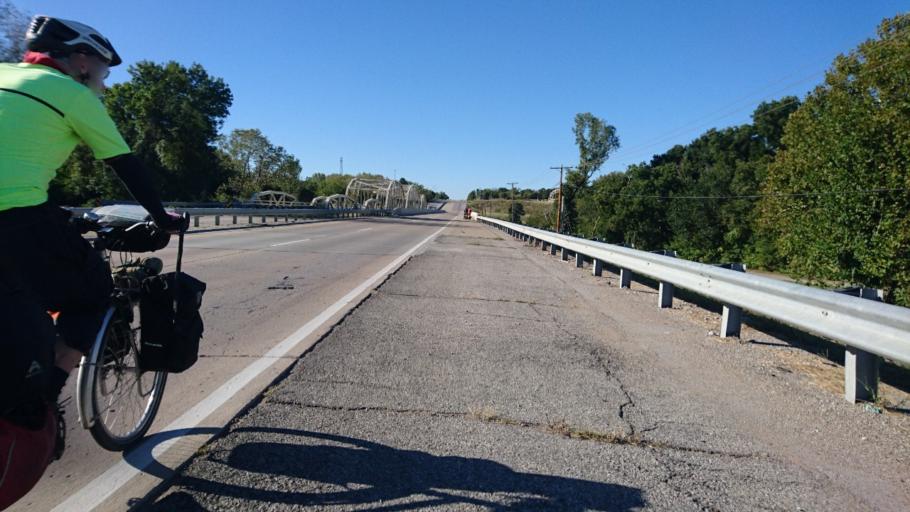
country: US
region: Oklahoma
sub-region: Rogers County
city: Catoosa
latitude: 36.2110
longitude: -95.7240
